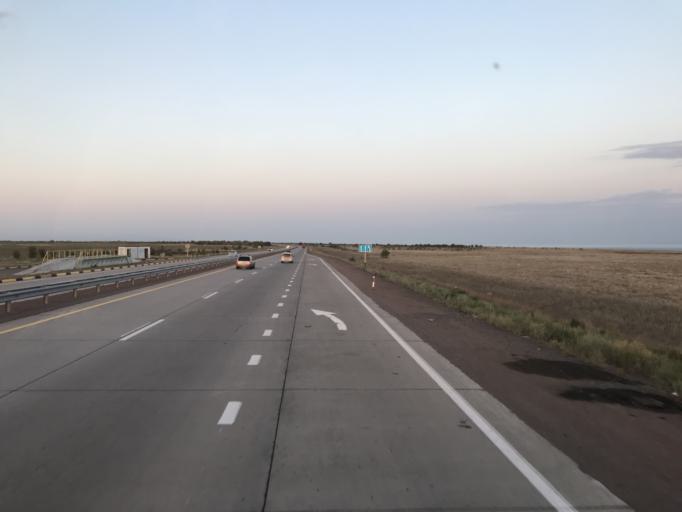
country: KZ
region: Almaty Oblysy
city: Kapshagay
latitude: 43.9238
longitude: 77.1675
